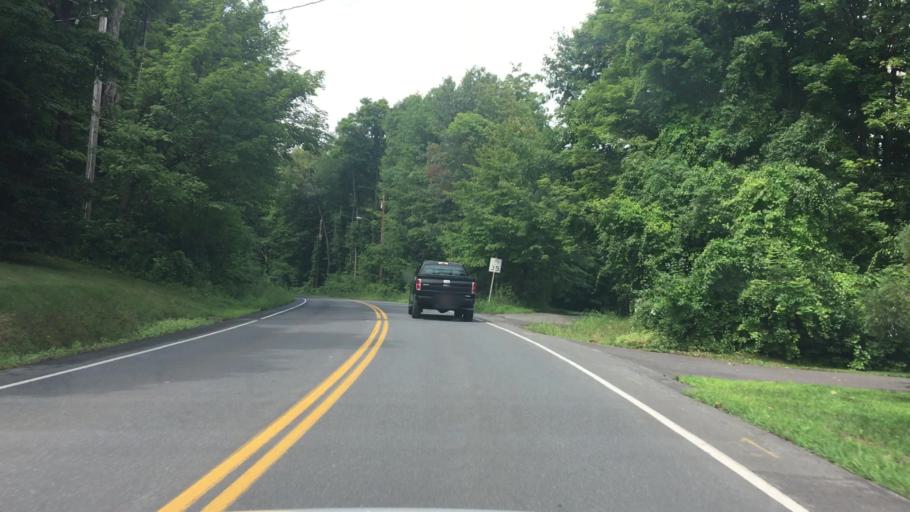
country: US
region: New York
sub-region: Rensselaer County
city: Wynantskill
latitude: 42.6969
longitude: -73.6644
